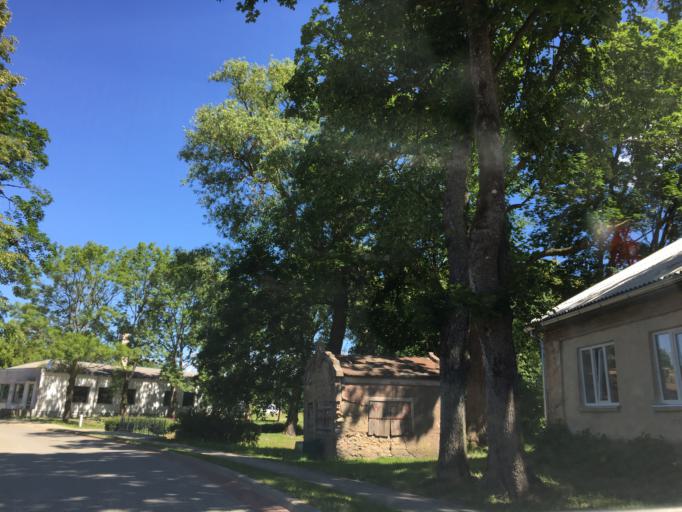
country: LV
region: Ventspils Rajons
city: Piltene
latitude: 57.2259
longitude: 21.6762
